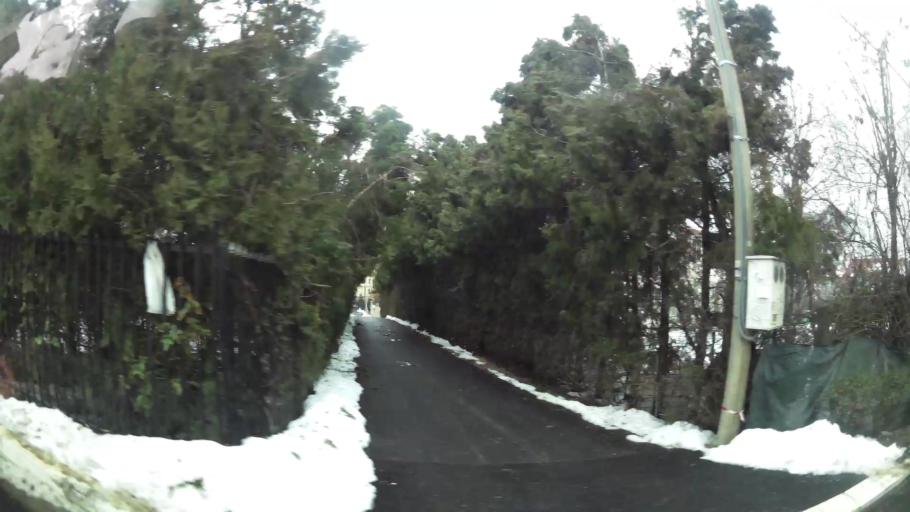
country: RS
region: Central Serbia
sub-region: Belgrade
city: Zvezdara
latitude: 44.7607
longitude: 20.5040
